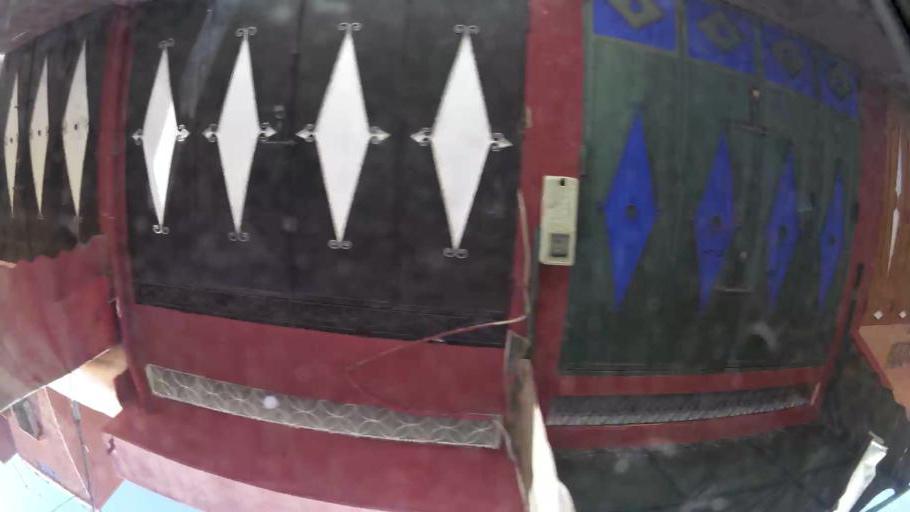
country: MA
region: Marrakech-Tensift-Al Haouz
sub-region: Marrakech
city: Marrakesh
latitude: 31.6571
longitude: -7.9975
